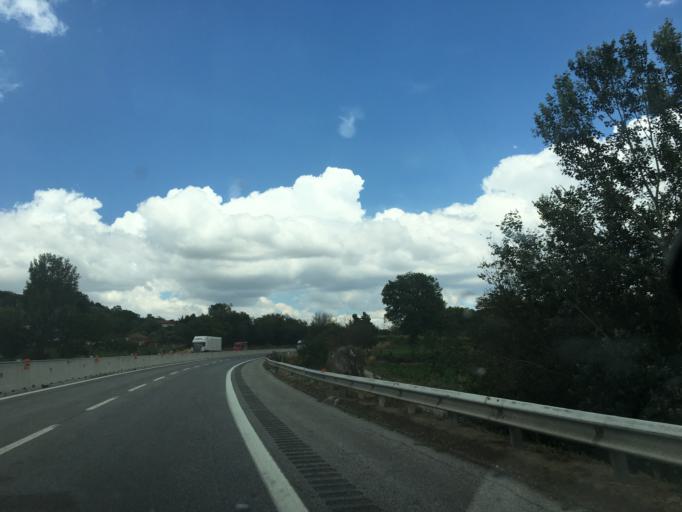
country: IT
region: Campania
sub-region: Provincia di Avellino
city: Passo di Mirabella-Pianopantano
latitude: 41.0601
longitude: 15.0375
